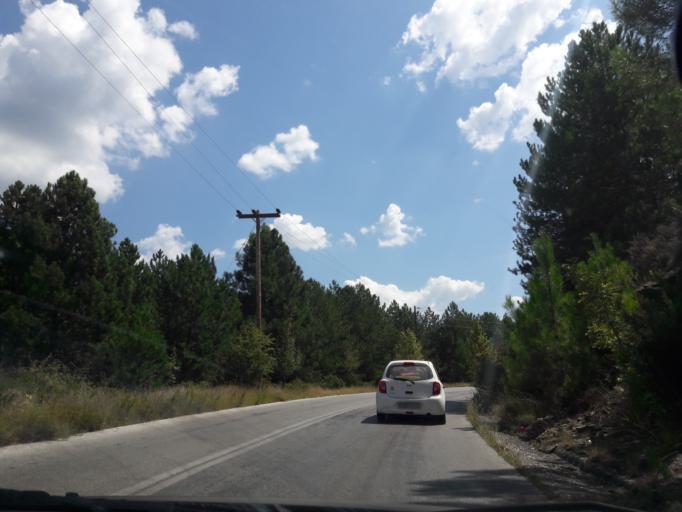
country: GR
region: Central Macedonia
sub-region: Nomos Chalkidikis
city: Polygyros
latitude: 40.3678
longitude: 23.4961
